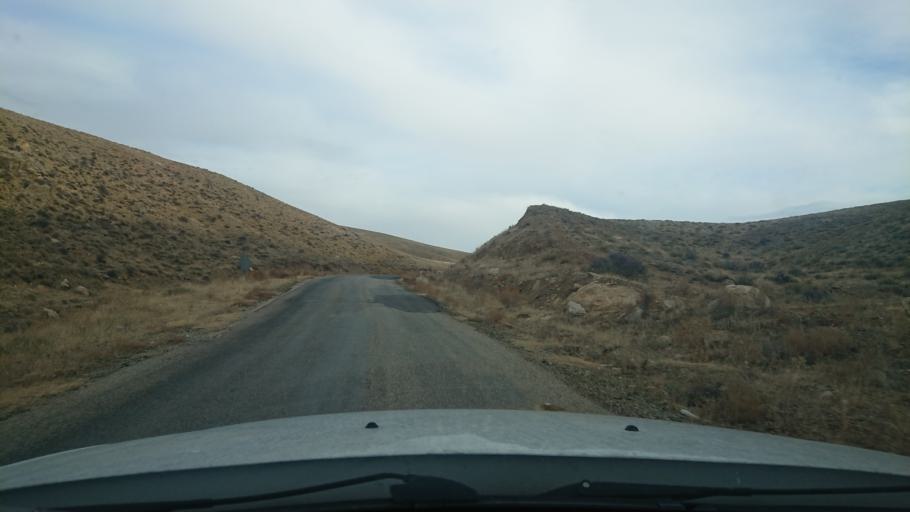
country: TR
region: Aksaray
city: Acipinar
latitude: 38.6262
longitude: 33.7998
